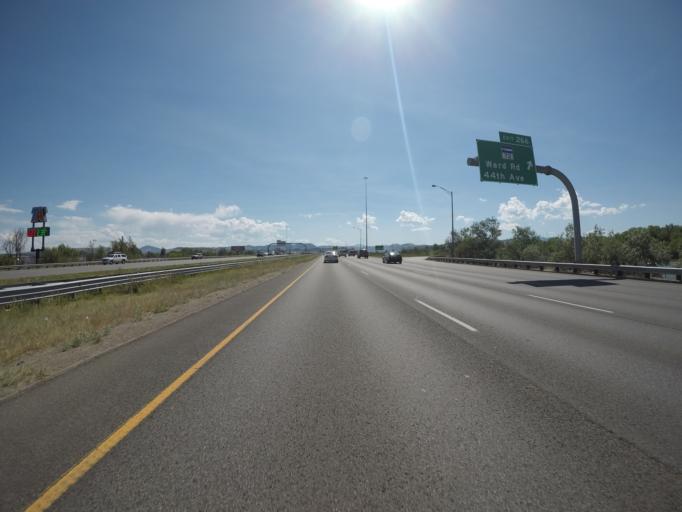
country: US
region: Colorado
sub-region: Jefferson County
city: Applewood
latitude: 39.7813
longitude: -105.1341
